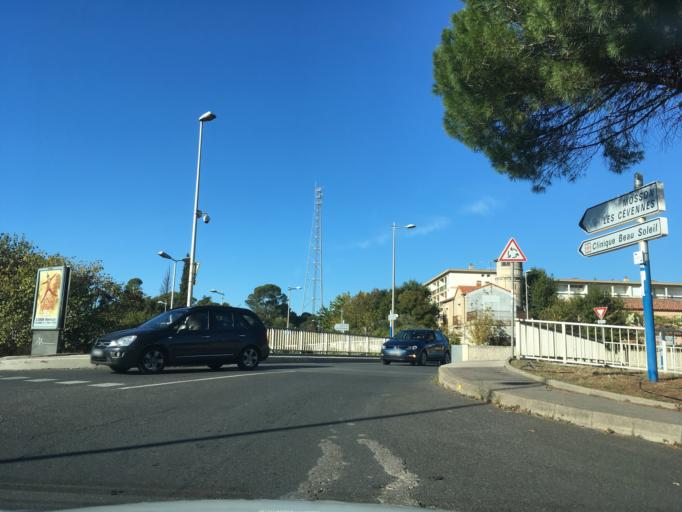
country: FR
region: Languedoc-Roussillon
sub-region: Departement de l'Herault
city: Montpellier
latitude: 43.6085
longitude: 3.8479
